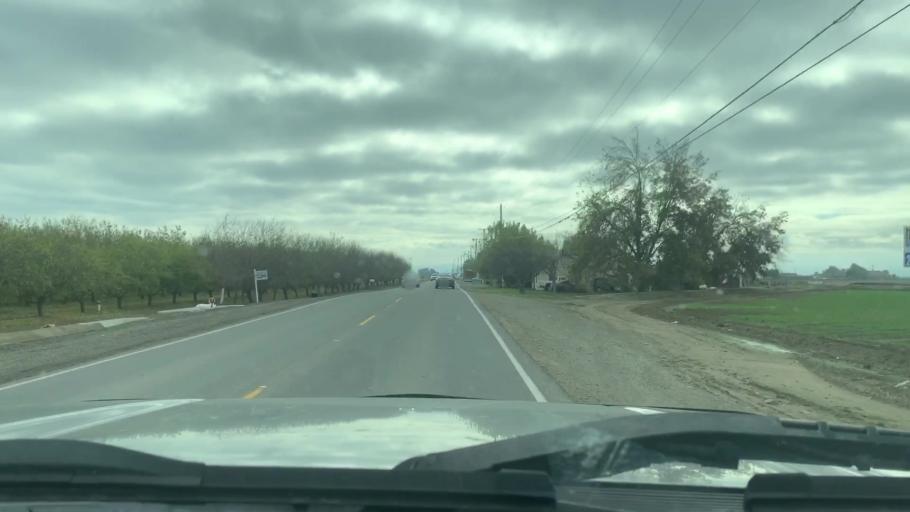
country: US
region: California
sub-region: Merced County
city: Los Banos
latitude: 37.0384
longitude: -120.8359
